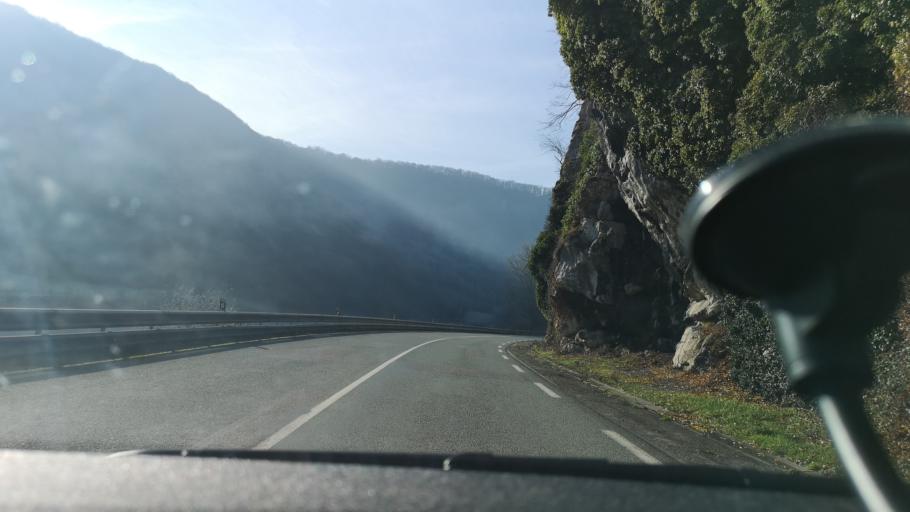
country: FR
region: Franche-Comte
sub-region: Departement du Doubs
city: Baume-les-Dames
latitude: 47.3568
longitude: 6.3924
